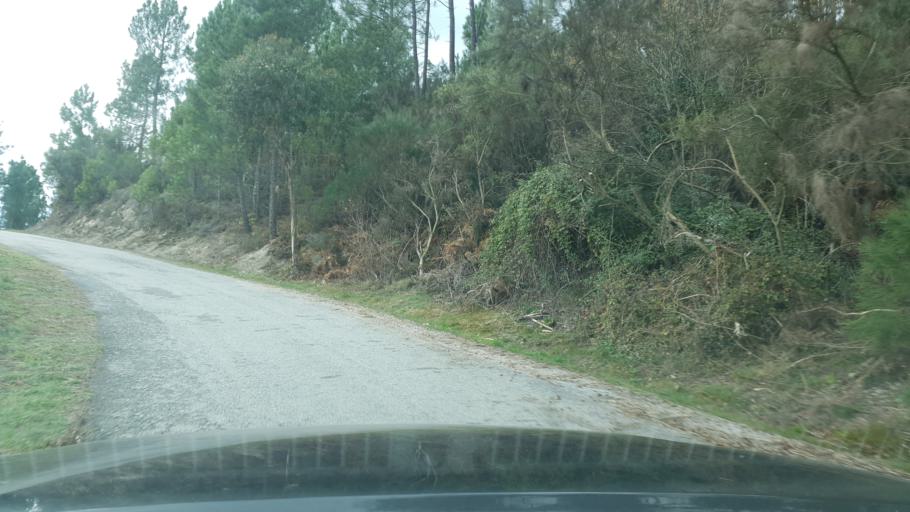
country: PT
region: Viseu
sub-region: Castro Daire
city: Castro Daire
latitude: 40.8807
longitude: -8.0038
